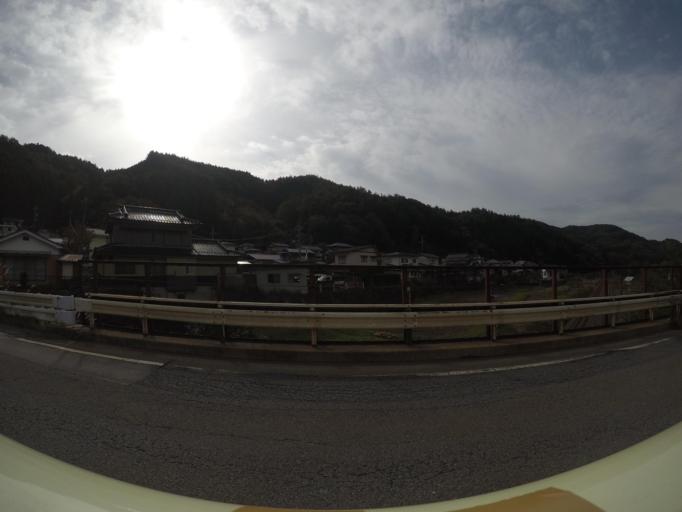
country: JP
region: Nagano
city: Ina
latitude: 35.8615
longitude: 137.7236
